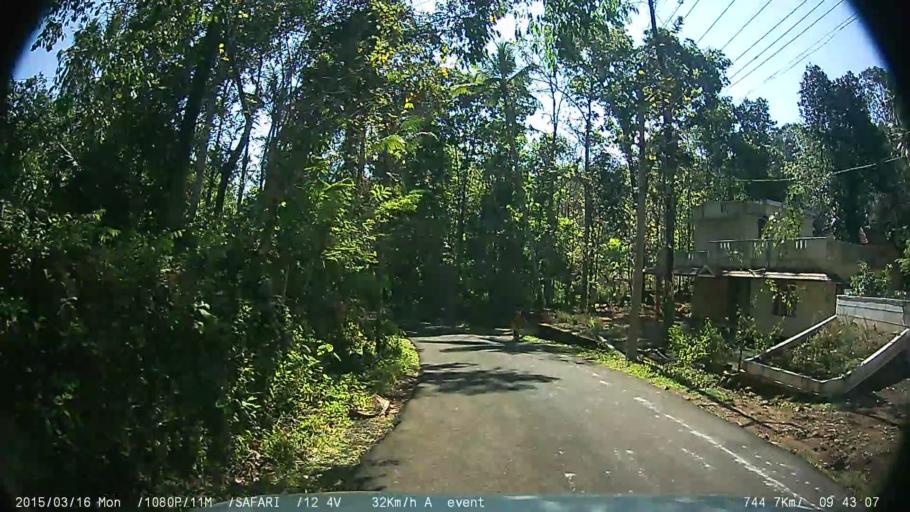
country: IN
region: Kerala
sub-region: Kottayam
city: Palackattumala
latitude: 9.7884
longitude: 76.6055
